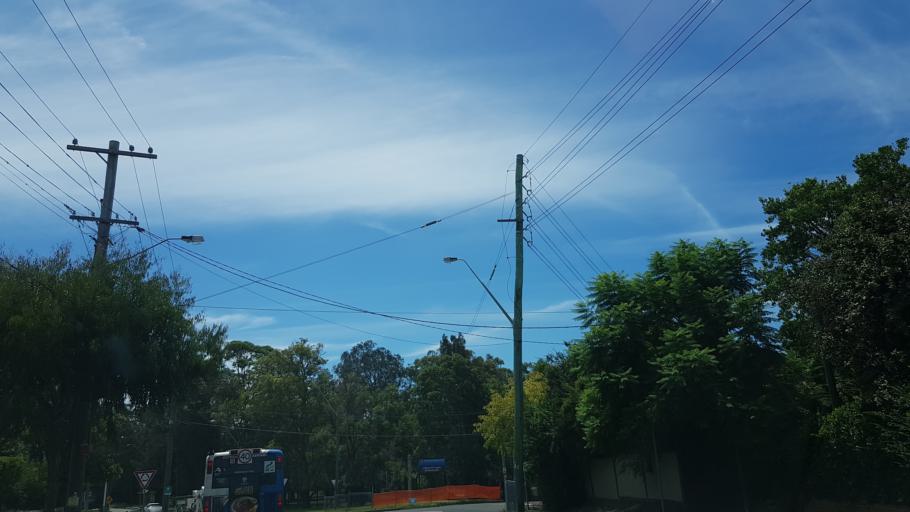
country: AU
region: New South Wales
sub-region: Pittwater
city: Bay View
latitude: -33.6711
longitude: 151.3024
